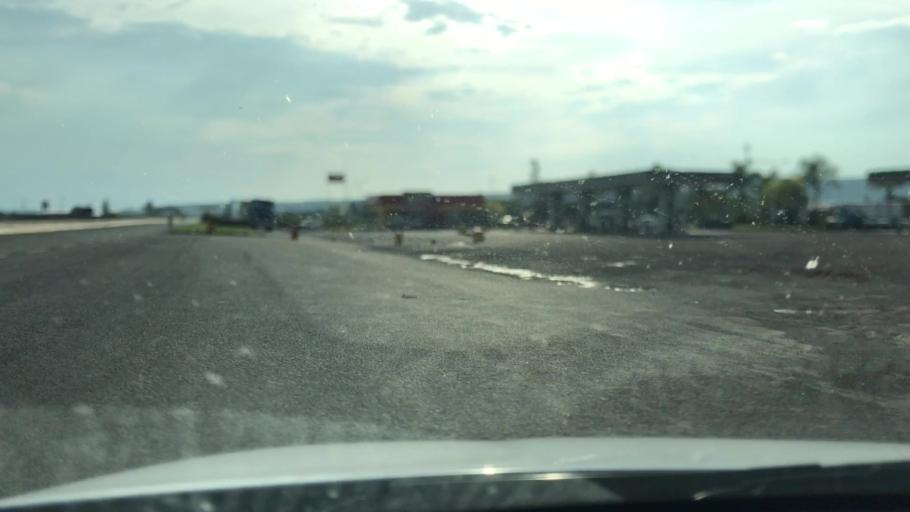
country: MX
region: Guanajuato
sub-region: Penjamo
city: Estacion la Piedad
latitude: 20.3889
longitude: -101.9344
